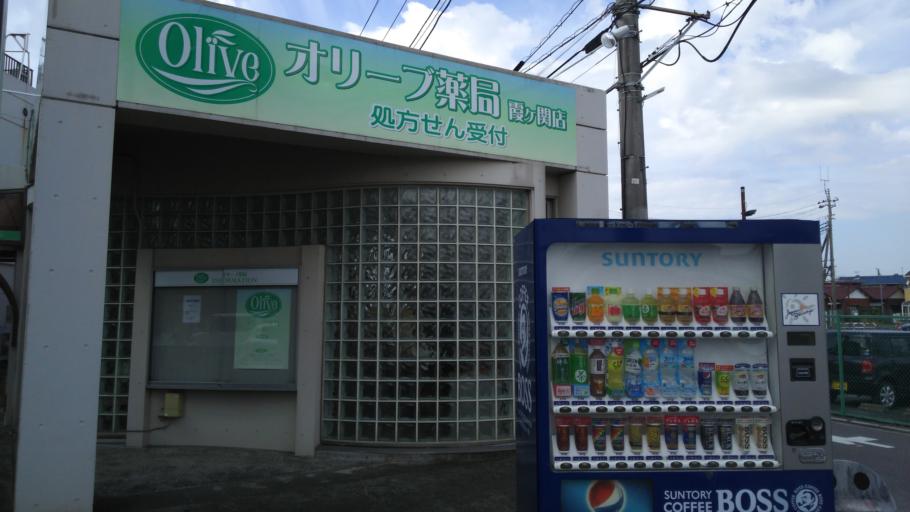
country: JP
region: Saitama
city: Kawagoe
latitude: 35.9264
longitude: 139.4424
